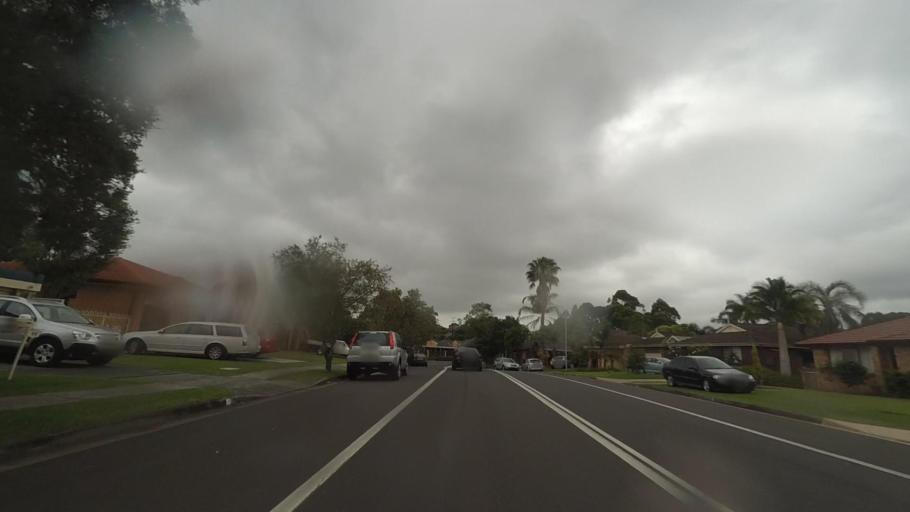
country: AU
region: New South Wales
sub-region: Wollongong
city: Cordeaux Heights
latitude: -34.4433
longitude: 150.8446
